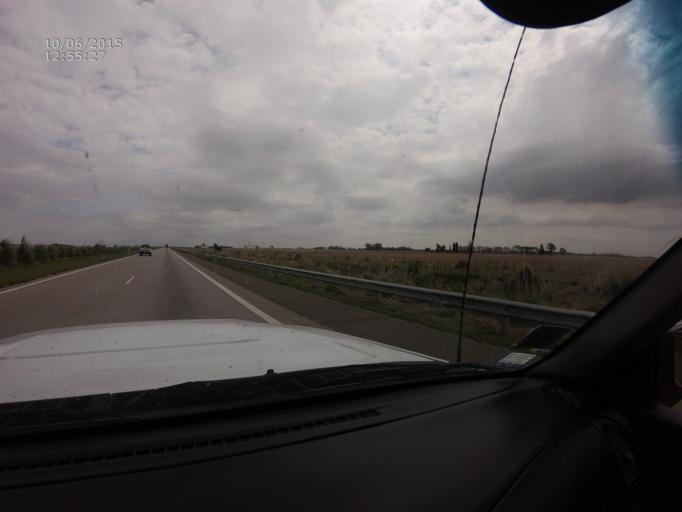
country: AR
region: Santa Fe
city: Armstrong
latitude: -32.8116
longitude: -61.5940
